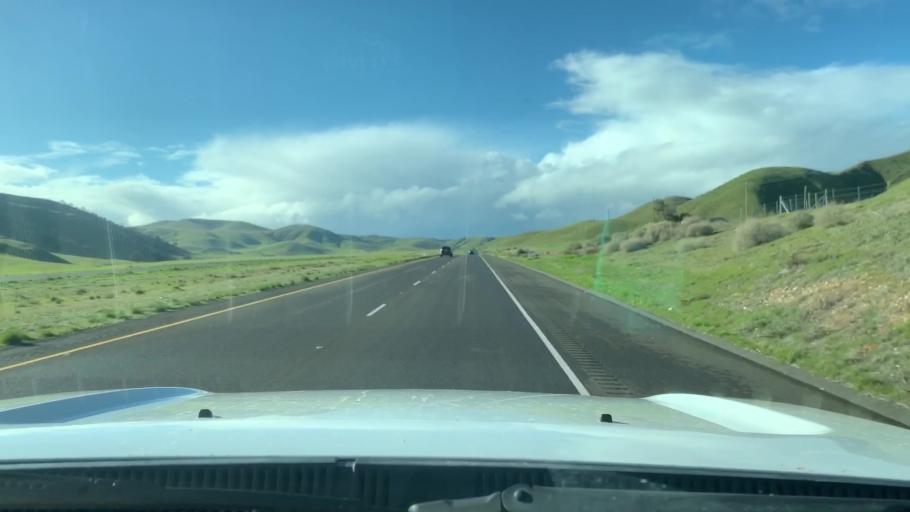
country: US
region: California
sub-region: San Luis Obispo County
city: Shandon
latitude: 35.7190
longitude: -120.1750
